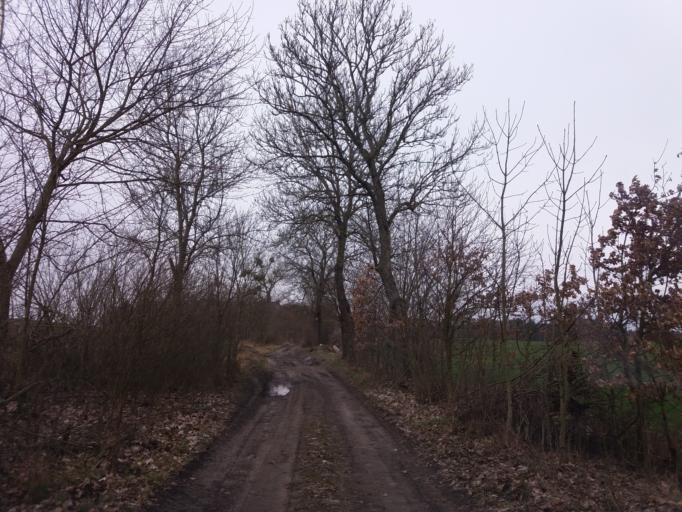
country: PL
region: West Pomeranian Voivodeship
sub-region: Powiat choszczenski
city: Bierzwnik
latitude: 53.1461
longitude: 15.6154
